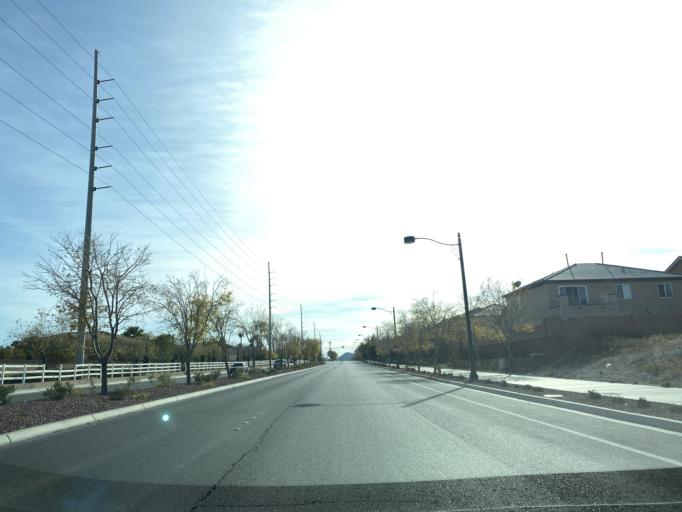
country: US
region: Nevada
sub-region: Clark County
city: Summerlin South
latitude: 36.3053
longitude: -115.3150
